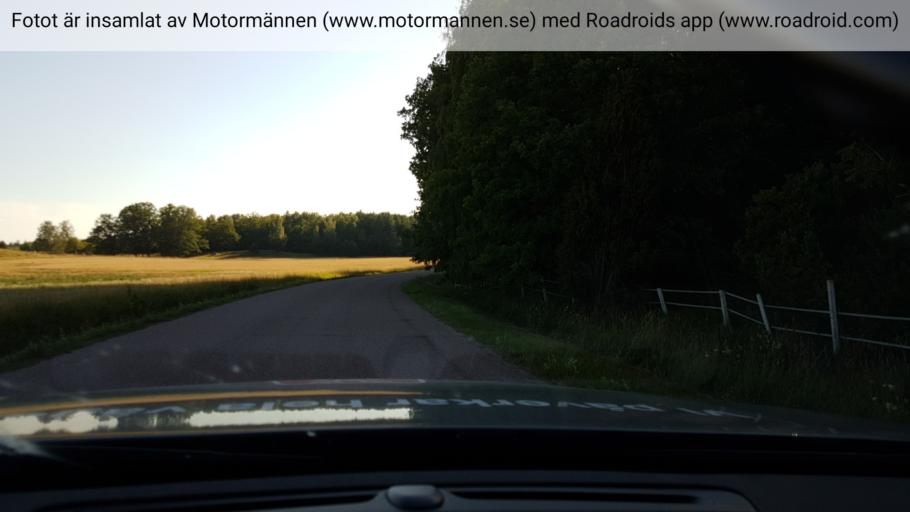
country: SE
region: Vaestmanland
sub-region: Surahammars Kommun
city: Surahammar
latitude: 59.7014
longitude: 16.1776
